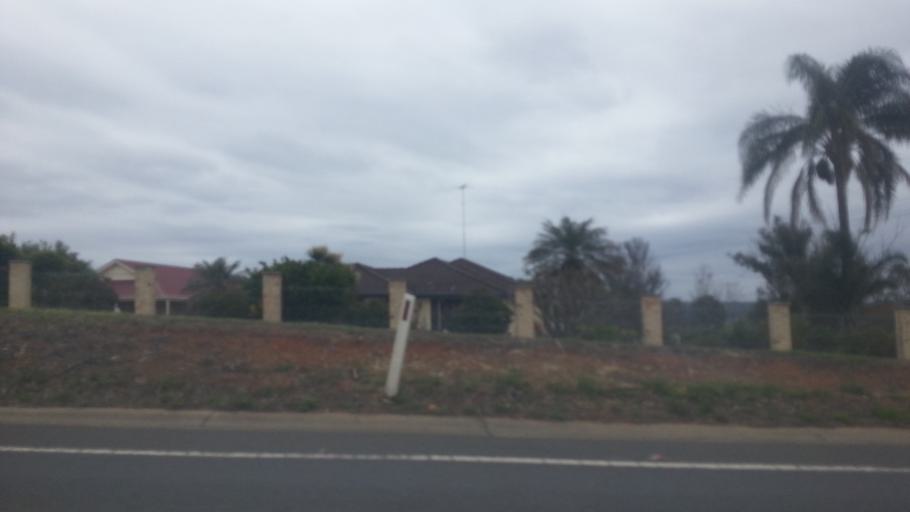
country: AU
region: New South Wales
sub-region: Penrith Municipality
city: Mulgoa
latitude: -33.8372
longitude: 150.6832
